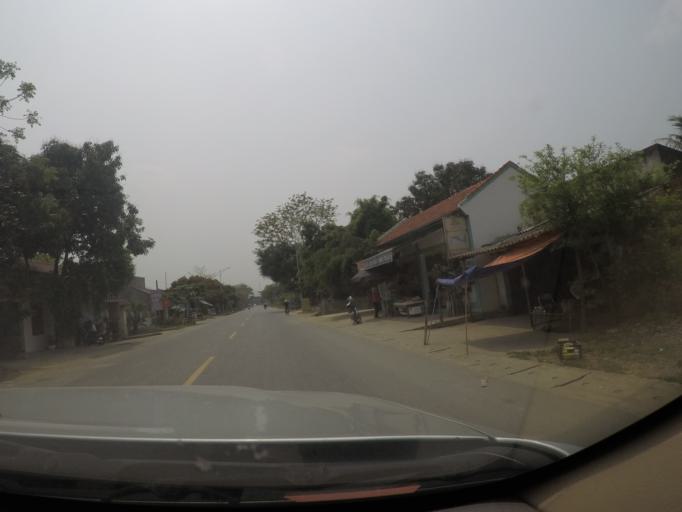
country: VN
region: Thanh Hoa
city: Thi Tran Cam Thuy
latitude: 20.2004
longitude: 105.4765
